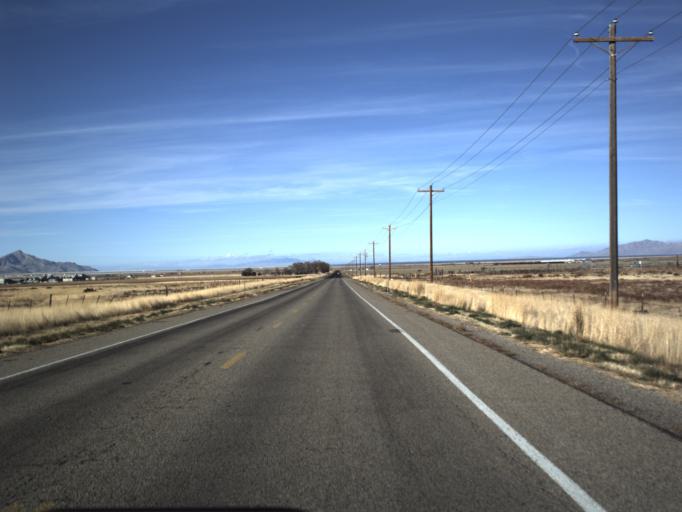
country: US
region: Utah
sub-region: Tooele County
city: Erda
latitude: 40.5900
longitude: -112.3703
